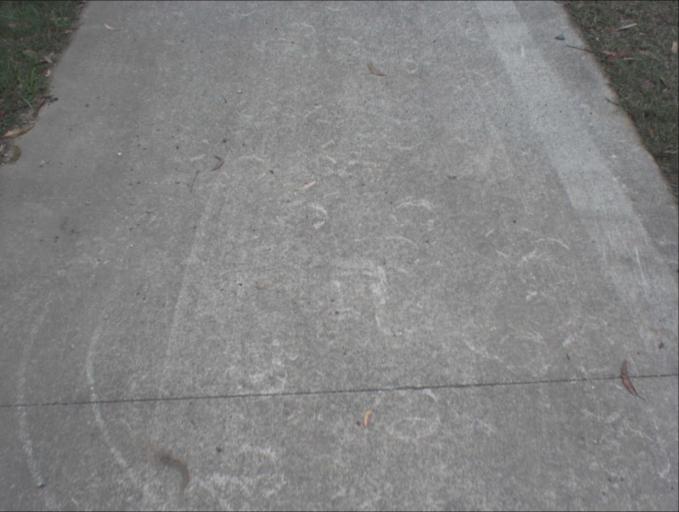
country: AU
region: Queensland
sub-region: Logan
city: Logan Reserve
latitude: -27.6988
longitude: 153.0769
